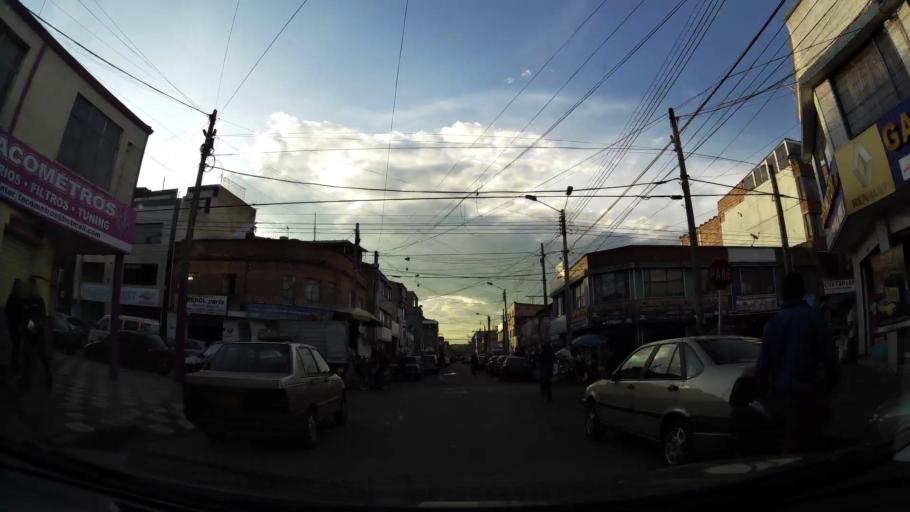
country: CO
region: Bogota D.C.
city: Bogota
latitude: 4.6575
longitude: -74.0727
